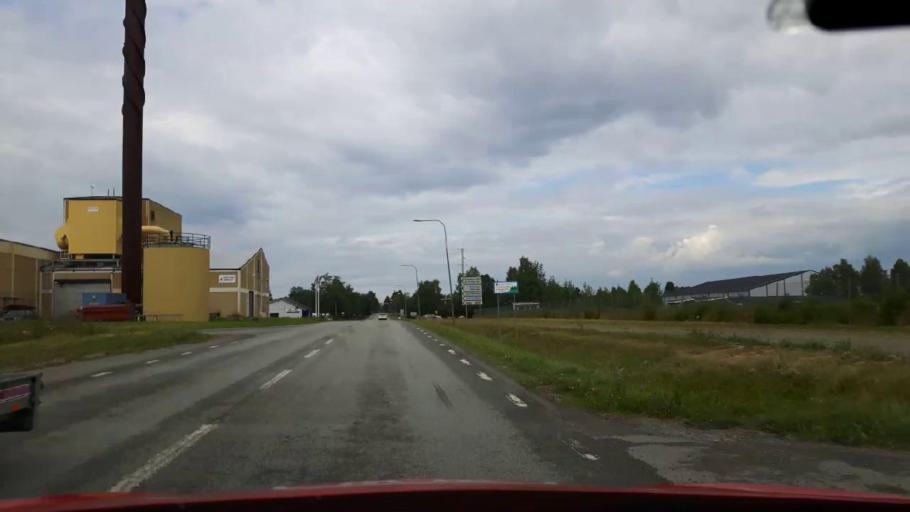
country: SE
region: Jaemtland
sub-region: Stroemsunds Kommun
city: Stroemsund
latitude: 63.8469
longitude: 15.5714
